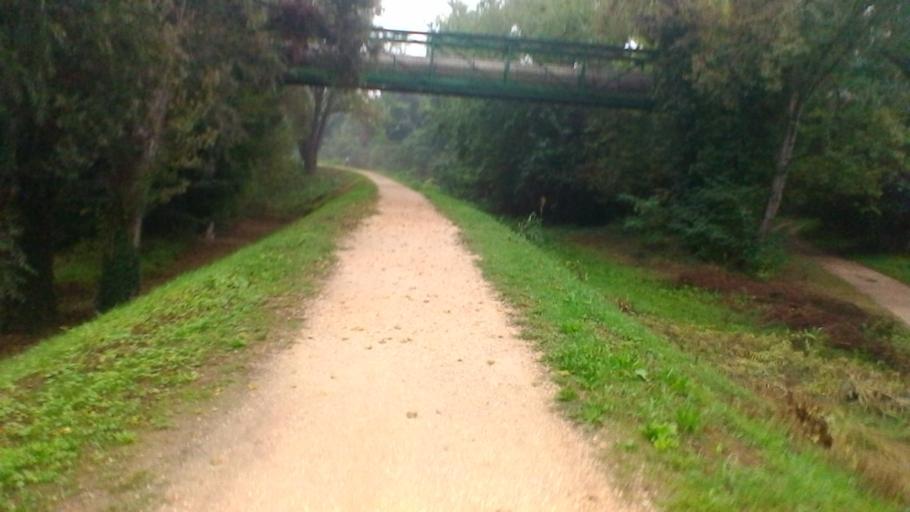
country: IT
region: Veneto
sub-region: Provincia di Verona
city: Verona
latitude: 45.4231
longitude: 10.9986
